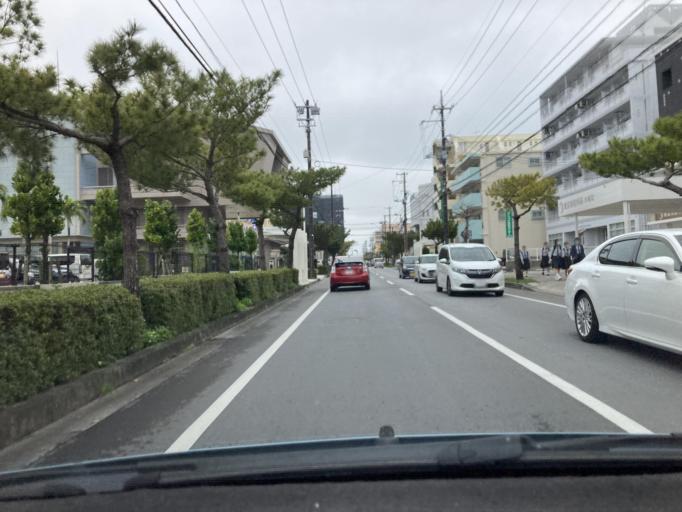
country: JP
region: Okinawa
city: Naha-shi
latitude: 26.2297
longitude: 127.6926
